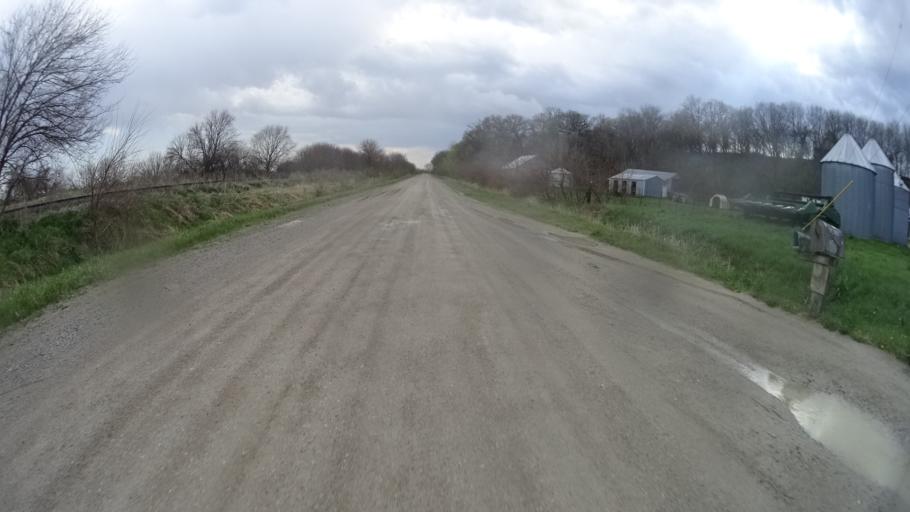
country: US
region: Nebraska
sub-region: Sarpy County
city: Offutt Air Force Base
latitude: 41.0881
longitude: -95.9155
